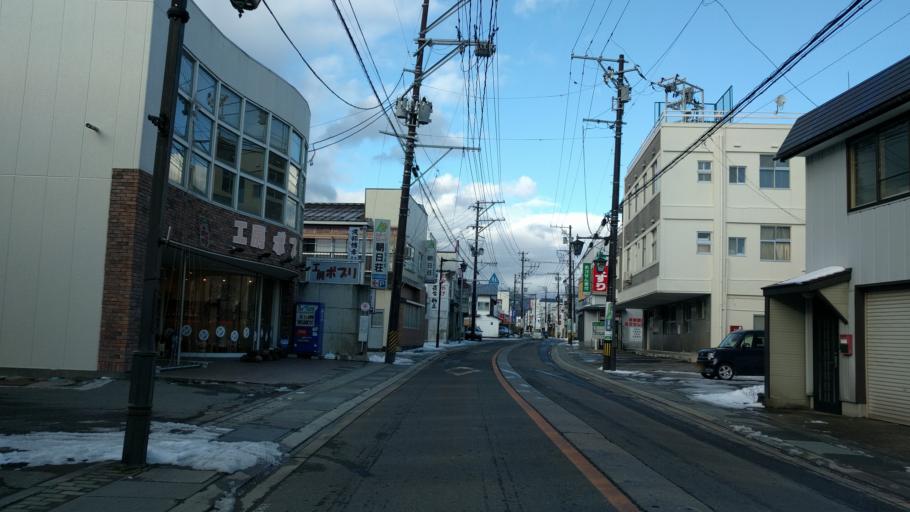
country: JP
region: Fukushima
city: Inawashiro
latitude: 37.5591
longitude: 140.1068
